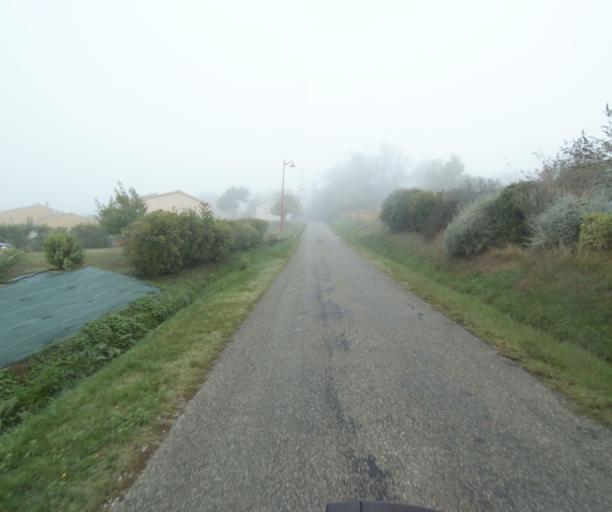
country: FR
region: Midi-Pyrenees
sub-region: Departement du Tarn-et-Garonne
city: Nohic
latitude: 43.9201
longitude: 1.4741
